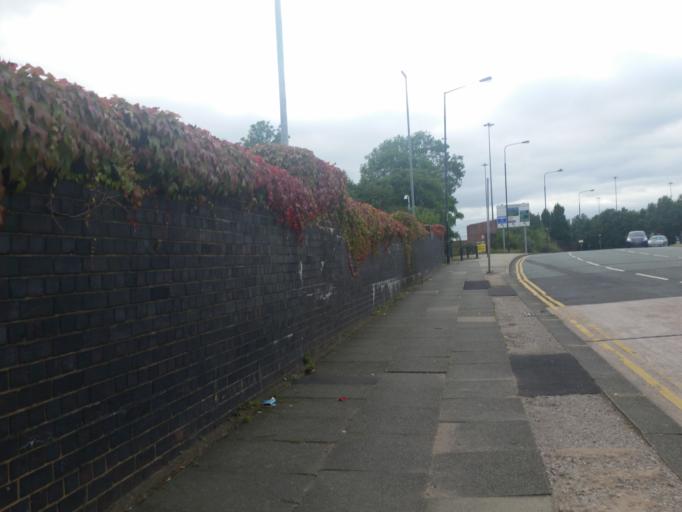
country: GB
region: England
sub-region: City and Borough of Salford
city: Salford
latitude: 53.4630
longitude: -2.2788
